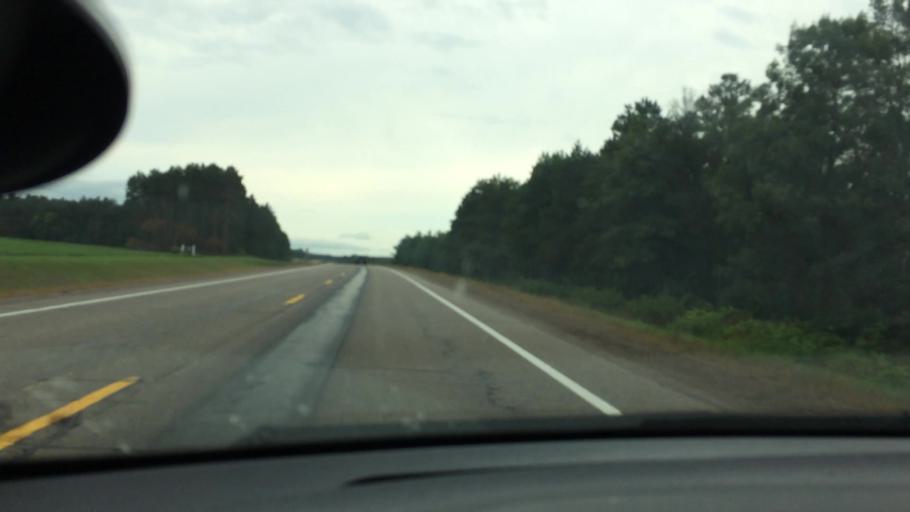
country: US
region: Wisconsin
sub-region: Eau Claire County
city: Augusta
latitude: 44.5855
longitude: -91.1211
